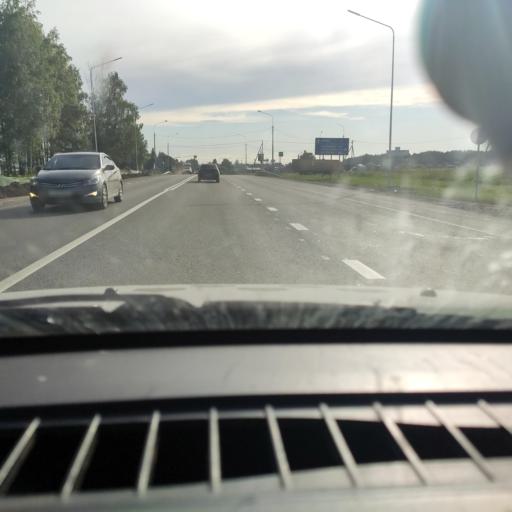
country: RU
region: Kirov
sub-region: Kirovo-Chepetskiy Rayon
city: Kirov
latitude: 58.6345
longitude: 49.8296
